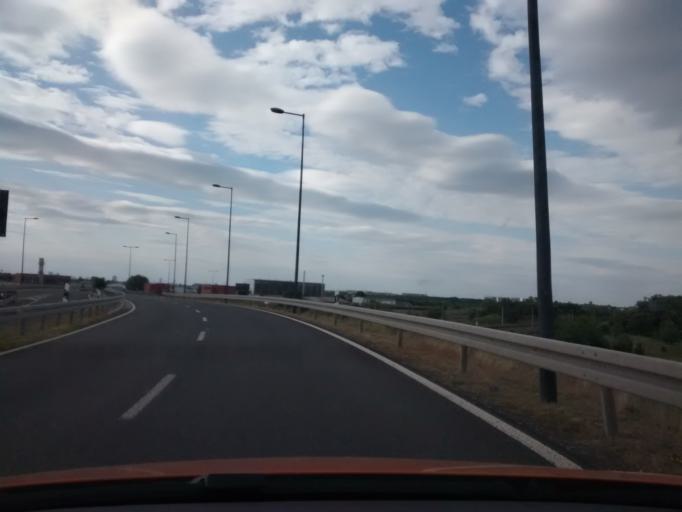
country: DE
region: Brandenburg
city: Schonefeld
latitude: 52.3706
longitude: 13.5334
